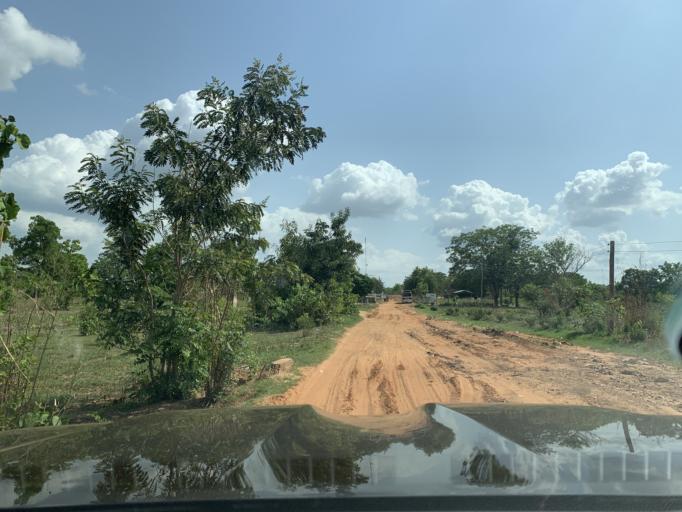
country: TG
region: Kara
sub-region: Prefecture de Bassar
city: Bassar
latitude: 9.3816
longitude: 0.5597
